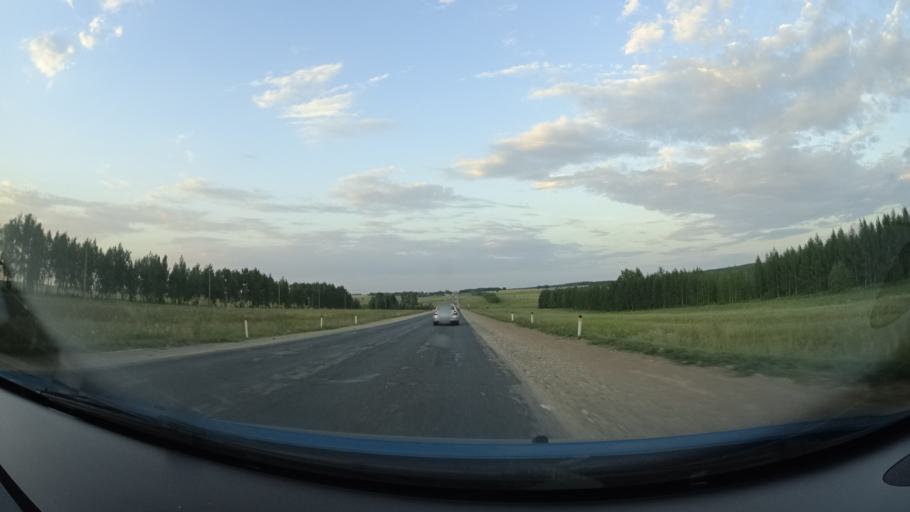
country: RU
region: Orenburg
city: Severnoye
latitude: 54.2304
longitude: 52.7658
